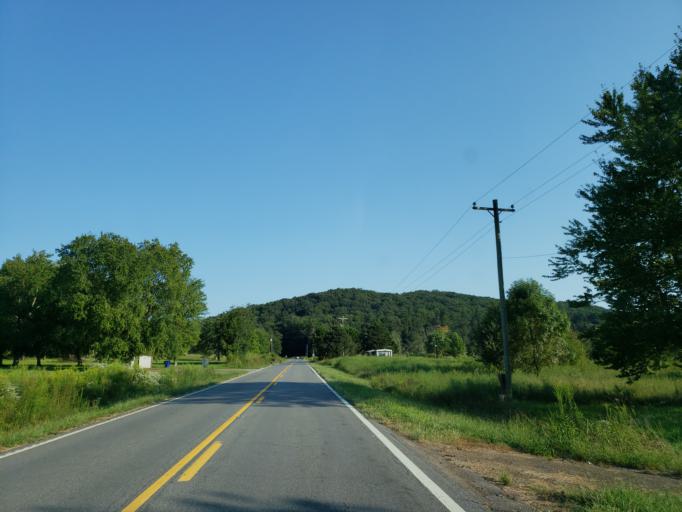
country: US
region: Tennessee
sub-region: Bradley County
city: Wildwood Lake
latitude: 35.0072
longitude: -84.7863
